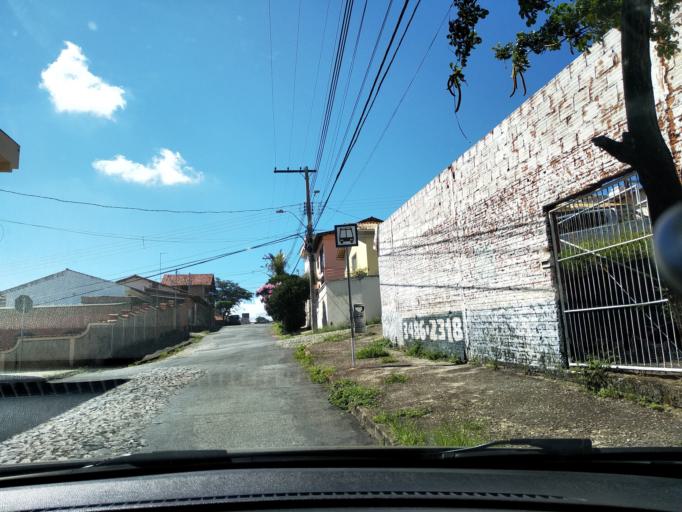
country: BR
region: Minas Gerais
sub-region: Belo Horizonte
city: Belo Horizonte
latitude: -19.8757
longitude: -43.9174
